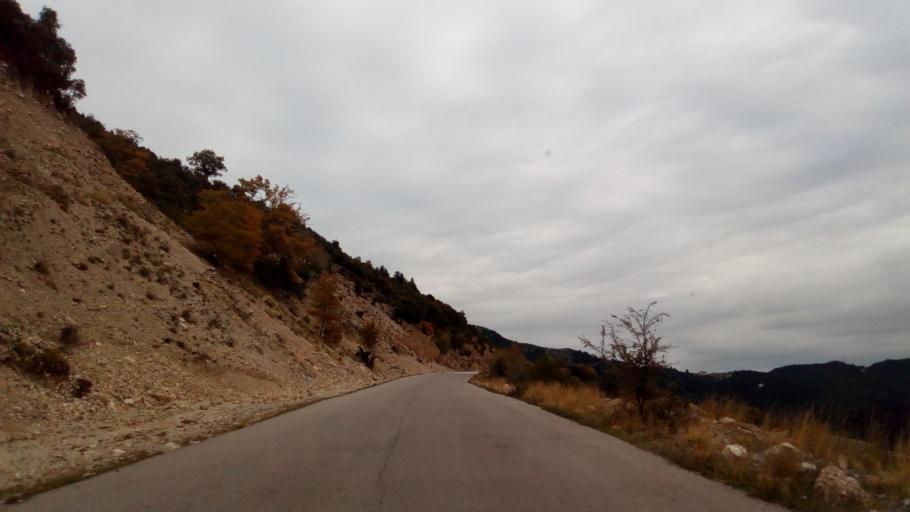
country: GR
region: West Greece
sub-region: Nomos Aitolias kai Akarnanias
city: Thermo
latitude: 38.6035
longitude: 21.8225
